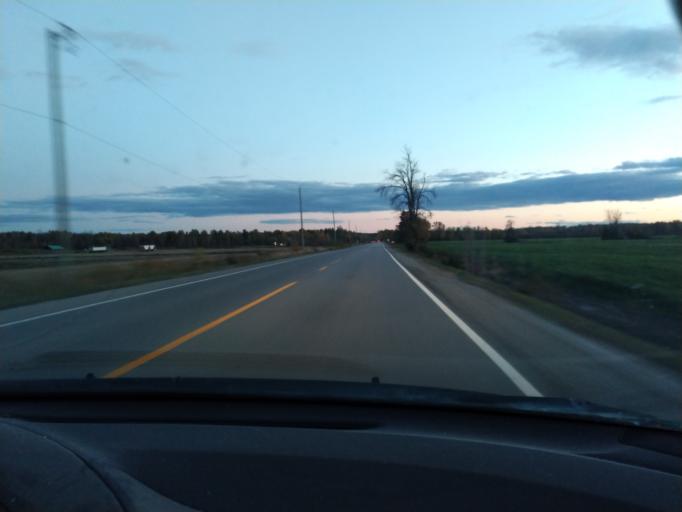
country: CA
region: Ontario
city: Bradford West Gwillimbury
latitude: 44.1957
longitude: -79.6638
